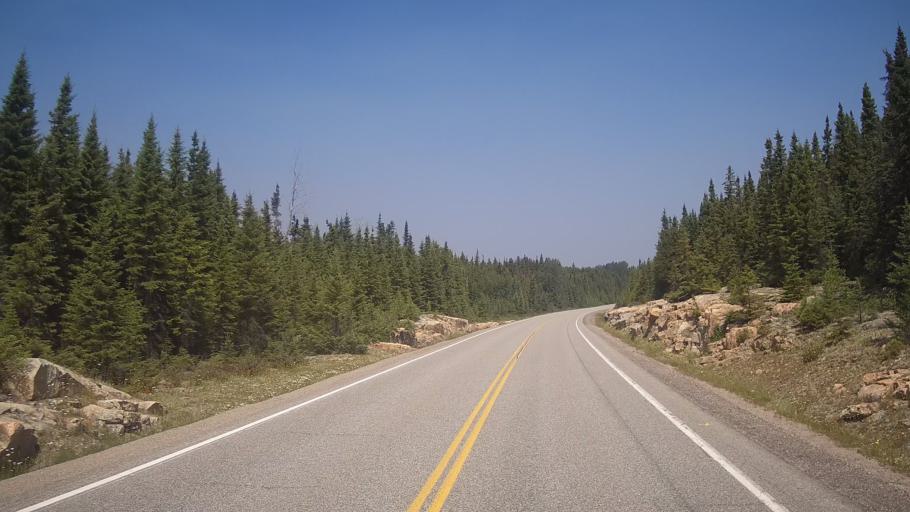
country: CA
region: Ontario
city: Timmins
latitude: 48.0743
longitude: -81.5941
